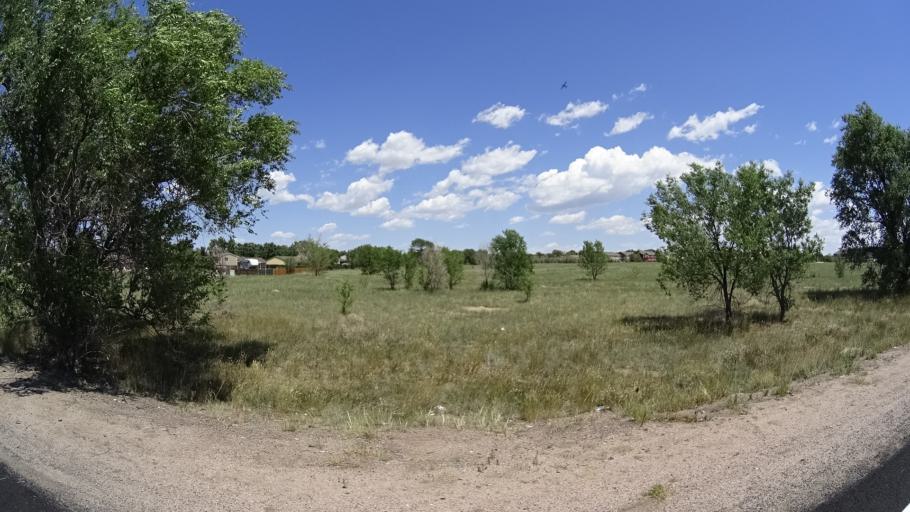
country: US
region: Colorado
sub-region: El Paso County
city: Stratmoor
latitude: 38.7882
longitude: -104.7420
